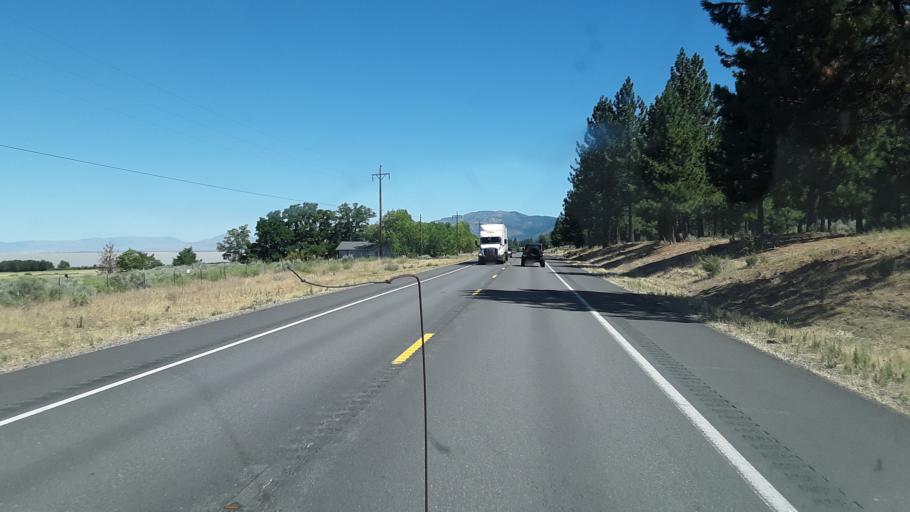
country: US
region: California
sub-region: Lassen County
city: Janesville
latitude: 40.2397
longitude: -120.4517
